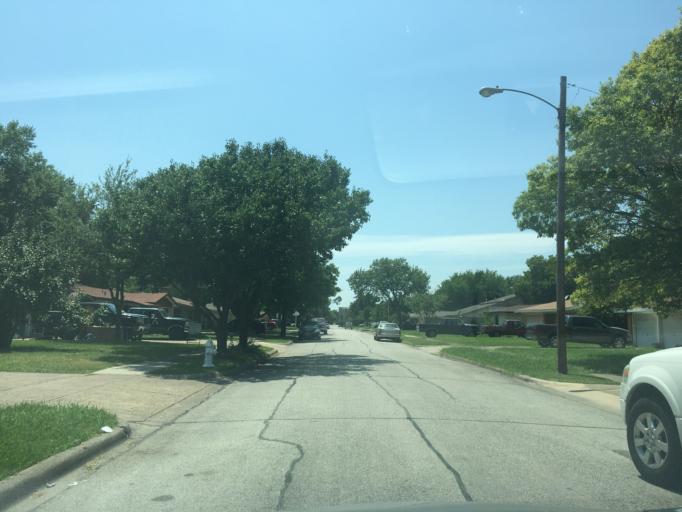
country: US
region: Texas
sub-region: Dallas County
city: Carrollton
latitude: 32.9372
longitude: -96.8740
